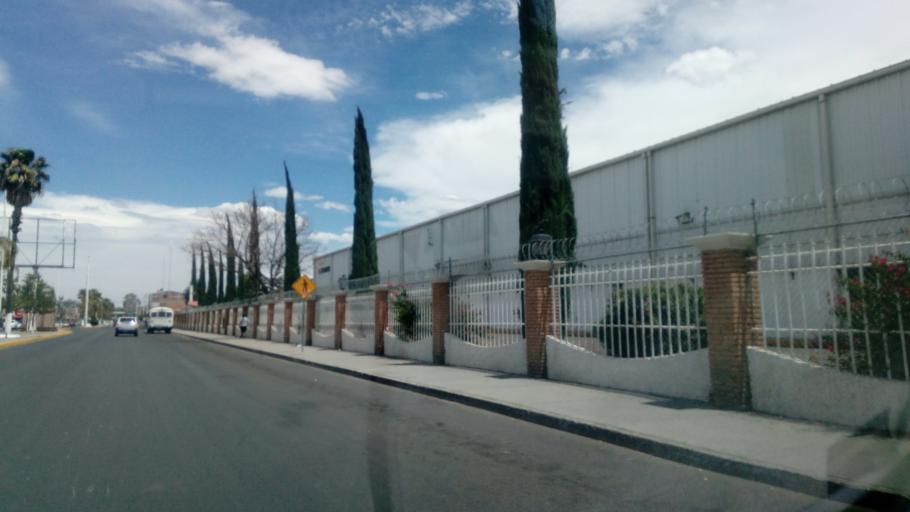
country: MX
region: Durango
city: Victoria de Durango
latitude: 23.9963
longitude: -104.6676
